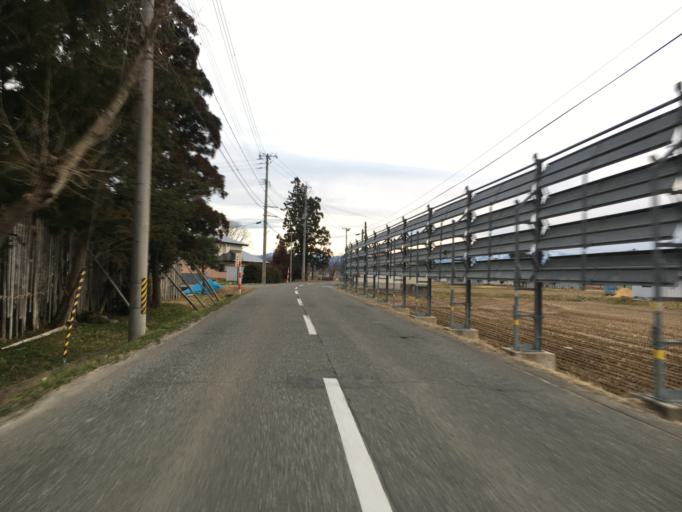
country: JP
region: Yamagata
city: Nagai
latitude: 38.0134
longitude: 140.0790
